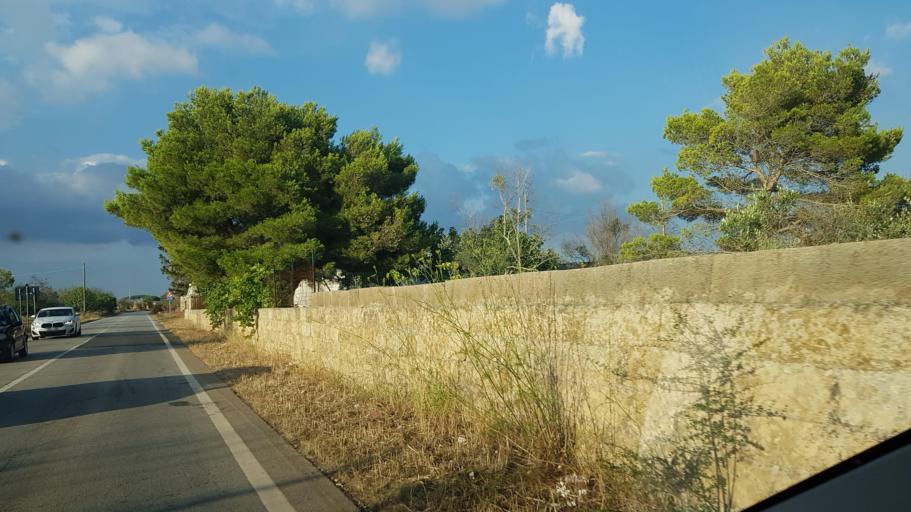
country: IT
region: Apulia
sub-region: Provincia di Lecce
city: Acquarica del Capo
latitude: 39.8774
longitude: 18.2276
